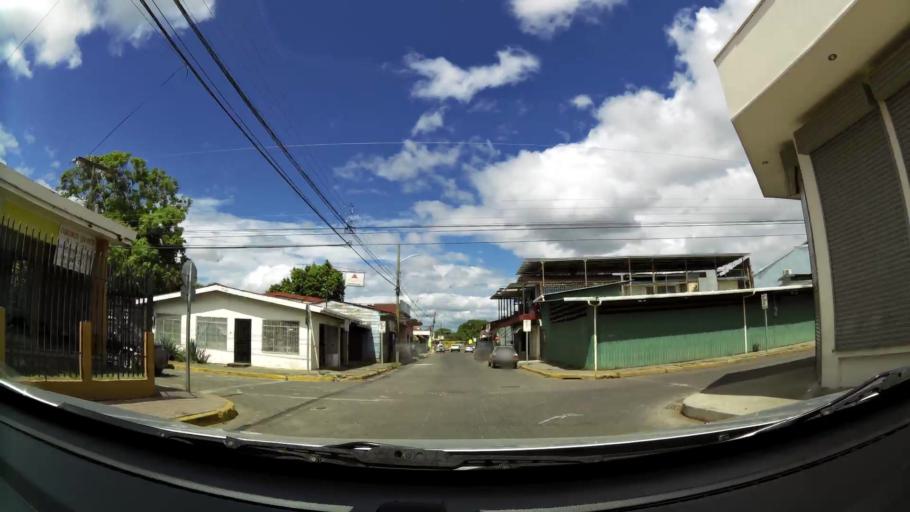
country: CR
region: Guanacaste
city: Santa Cruz
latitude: 10.2613
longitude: -85.5869
